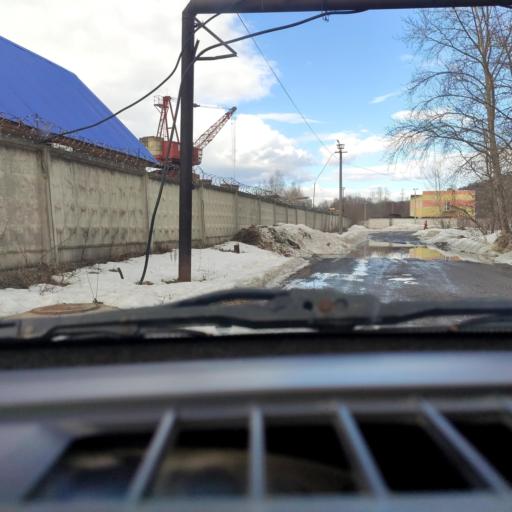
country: RU
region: Perm
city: Perm
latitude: 58.0779
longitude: 56.3460
